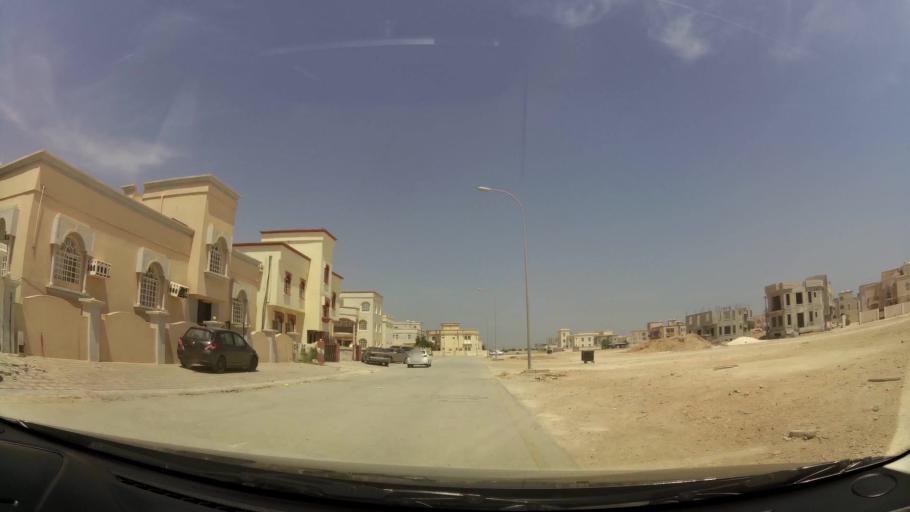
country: OM
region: Zufar
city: Salalah
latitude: 17.0611
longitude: 54.1606
